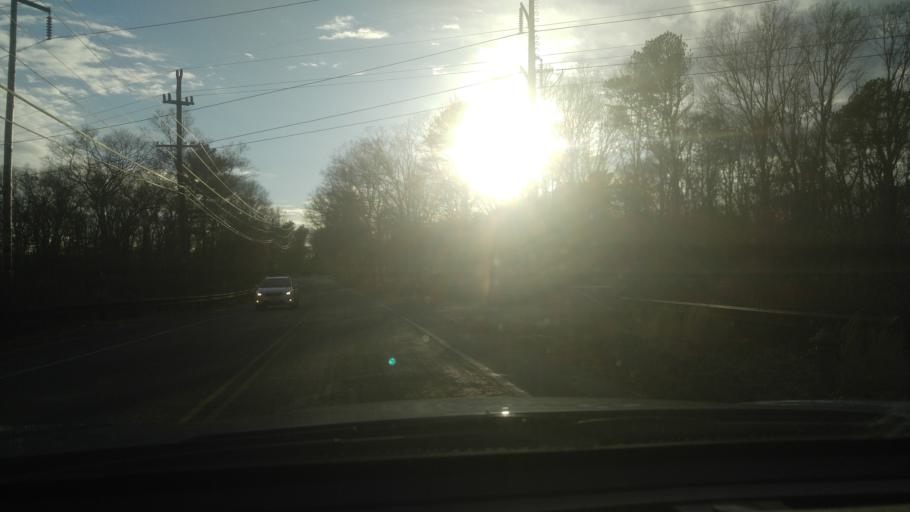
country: US
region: Rhode Island
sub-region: Washington County
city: Exeter
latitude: 41.5896
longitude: -71.4927
